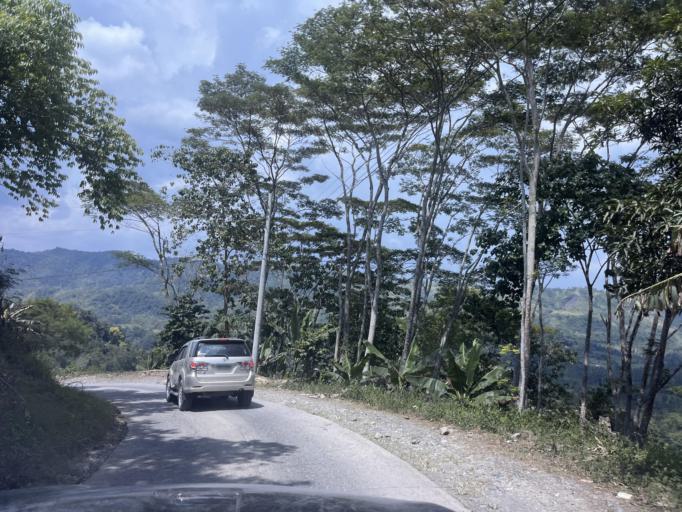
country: PH
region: Davao
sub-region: Province of Davao del Sur
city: Tamugan
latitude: 7.2904
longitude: 125.3403
